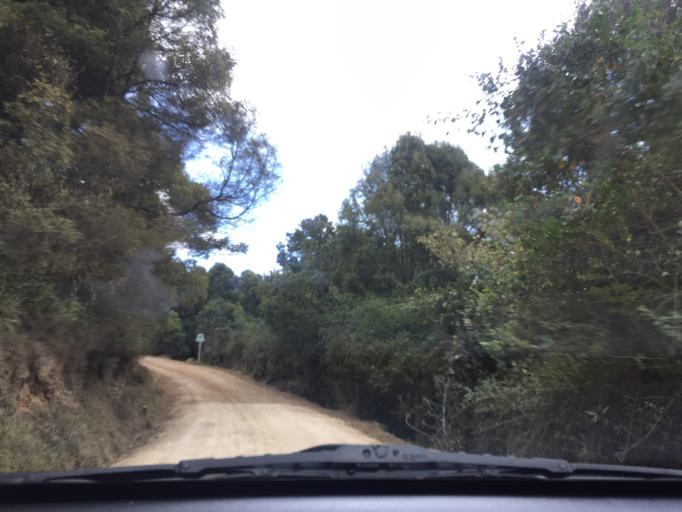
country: CO
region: Cundinamarca
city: Tabio
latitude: 4.9212
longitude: -74.1063
